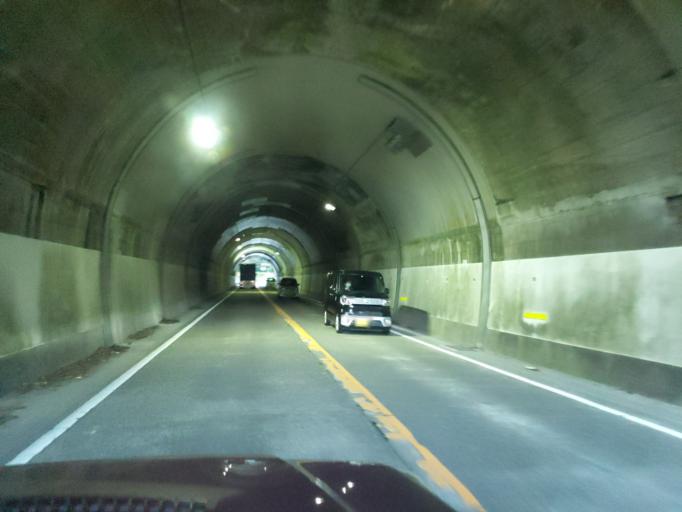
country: JP
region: Tokushima
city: Anan
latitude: 33.7162
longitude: 134.4842
